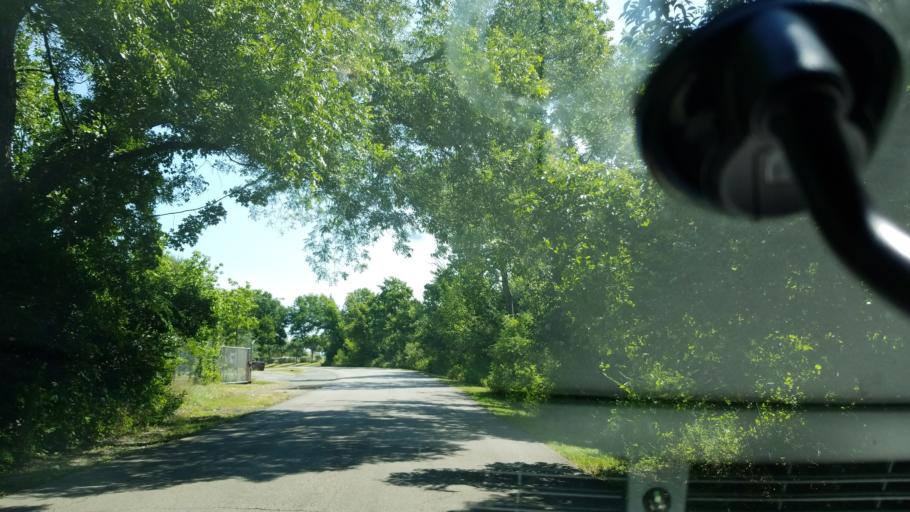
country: US
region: Texas
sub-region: Dallas County
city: Cockrell Hill
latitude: 32.7179
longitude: -96.8807
